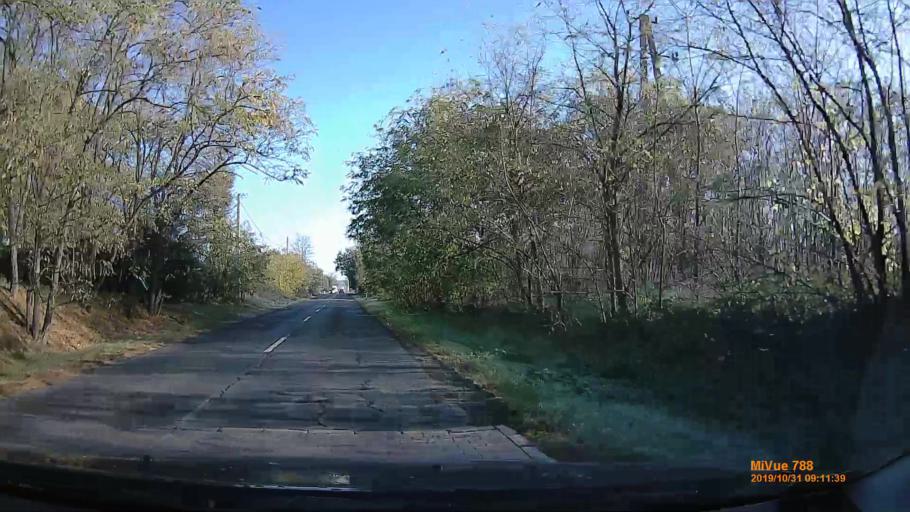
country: HU
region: Pest
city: Peteri
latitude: 47.3684
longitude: 19.3884
